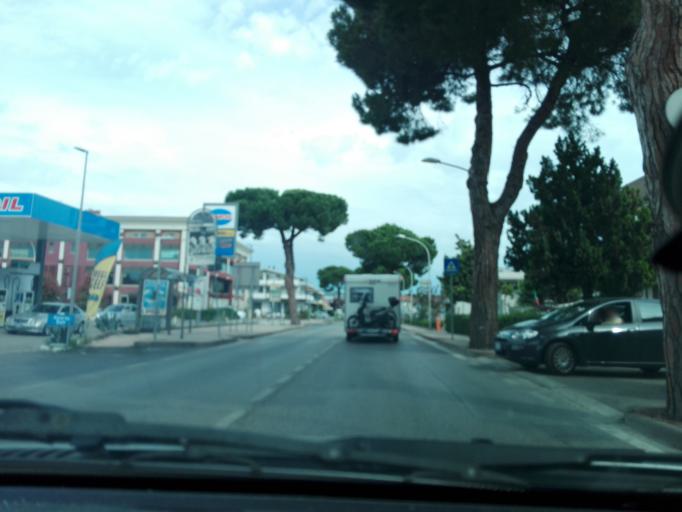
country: IT
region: Abruzzo
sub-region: Provincia di Pescara
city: San Martino Bassa
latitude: 42.5241
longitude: 14.1408
